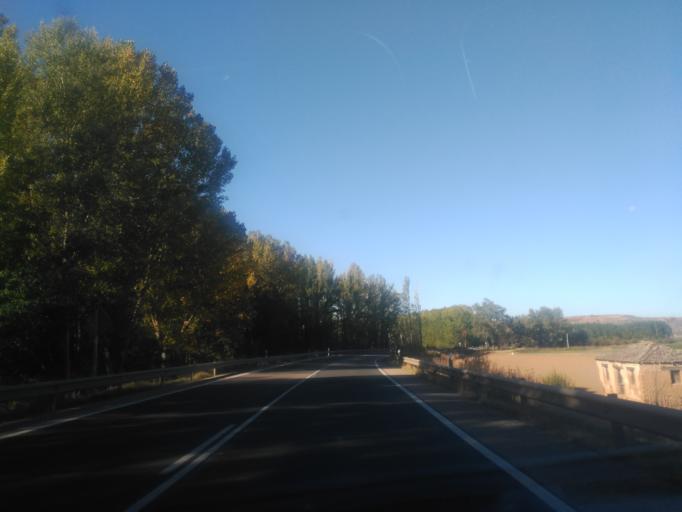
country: ES
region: Castille and Leon
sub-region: Provincia de Burgos
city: Fuentecen
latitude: 41.6306
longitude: -3.8471
